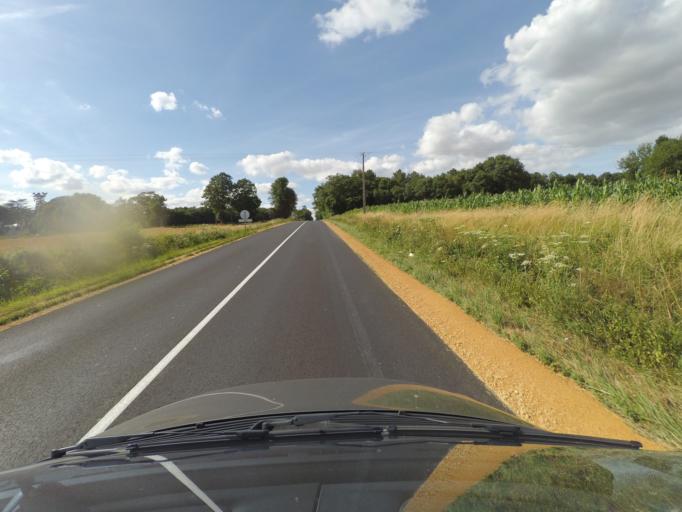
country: FR
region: Poitou-Charentes
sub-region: Departement de la Vienne
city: Saint-Gervais-les-Trois-Clochers
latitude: 46.9025
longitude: 0.4546
